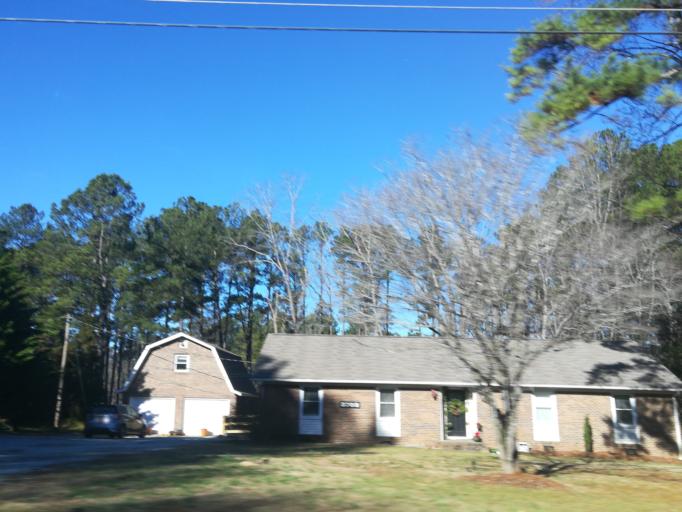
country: US
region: North Carolina
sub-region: Durham County
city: Durham
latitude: 36.0546
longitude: -78.9716
